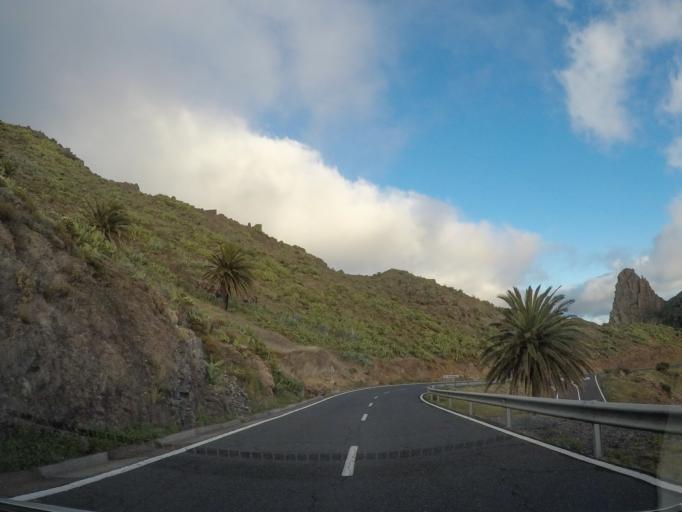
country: ES
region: Canary Islands
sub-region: Provincia de Santa Cruz de Tenerife
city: Alajero
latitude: 28.0822
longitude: -17.2453
